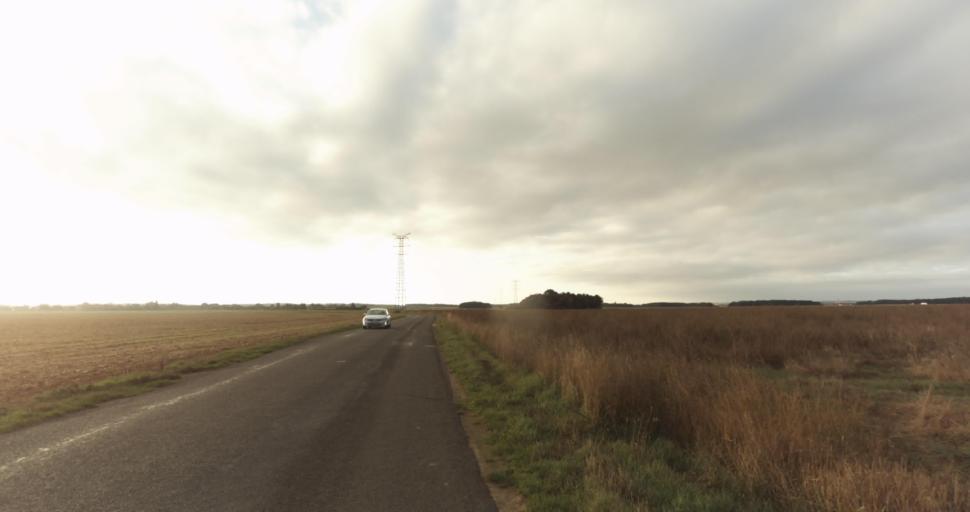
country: FR
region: Centre
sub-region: Departement d'Eure-et-Loir
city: Luray
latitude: 48.7036
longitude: 1.3847
